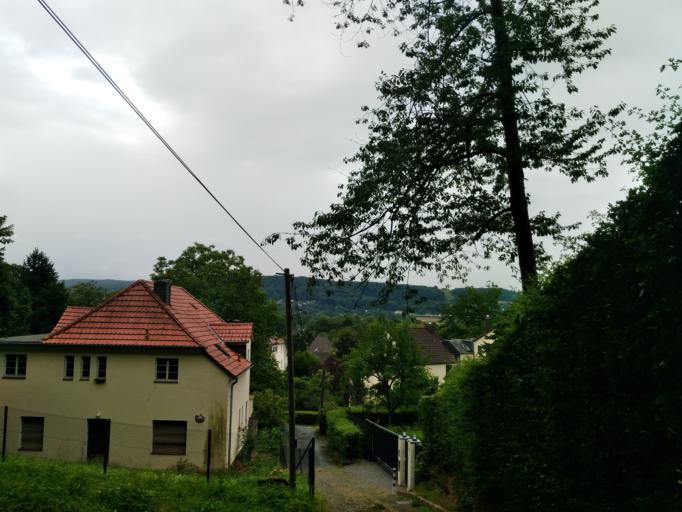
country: DE
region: North Rhine-Westphalia
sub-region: Regierungsbezirk Koln
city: Bad Honnef
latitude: 50.6578
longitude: 7.2205
